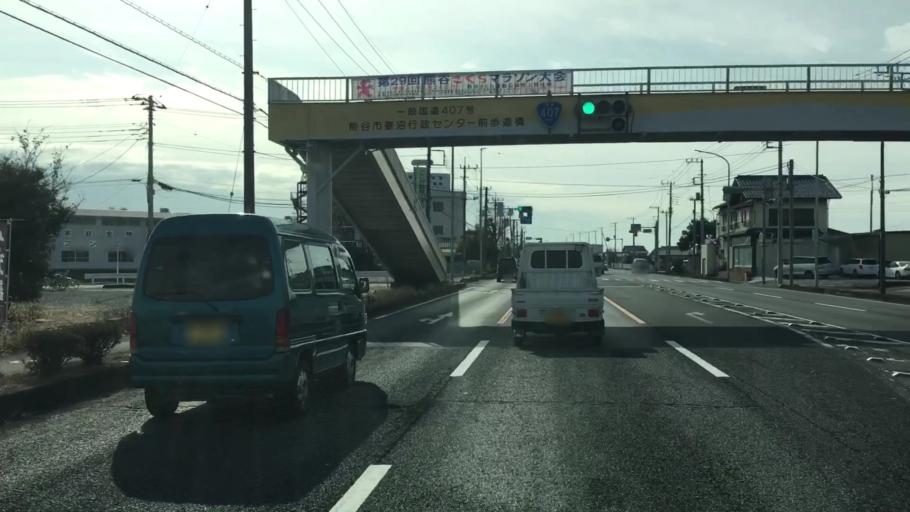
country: JP
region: Saitama
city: Menuma
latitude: 36.2233
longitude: 139.3692
